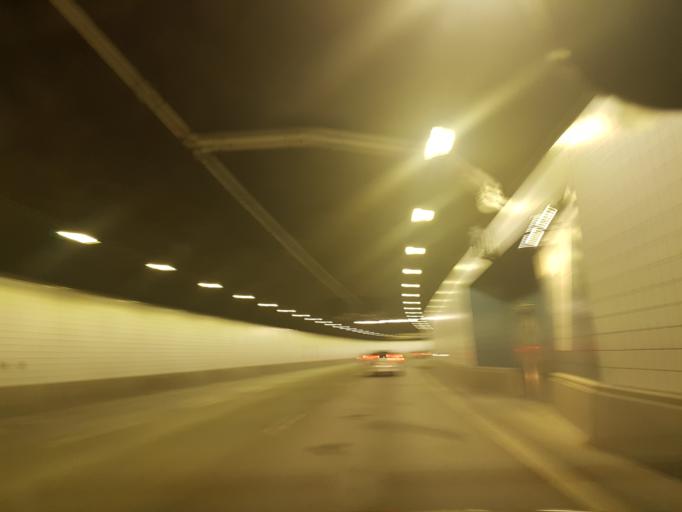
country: SE
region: Vaestra Goetaland
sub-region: Goteborg
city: Goeteborg
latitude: 57.7043
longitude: 11.9611
